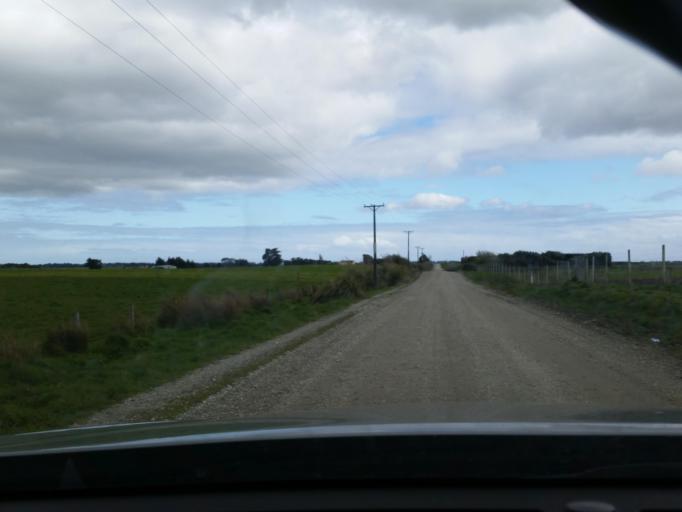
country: NZ
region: Southland
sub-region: Invercargill City
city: Invercargill
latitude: -46.4426
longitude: 168.5062
